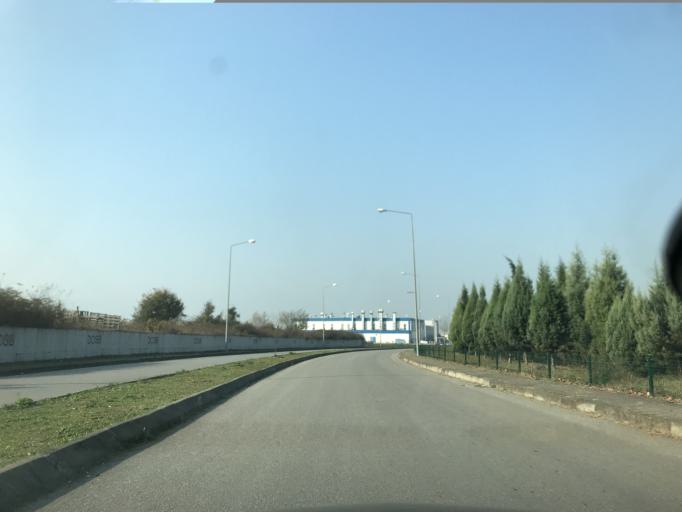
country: TR
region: Duzce
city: Duzce
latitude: 40.7839
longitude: 31.1520
